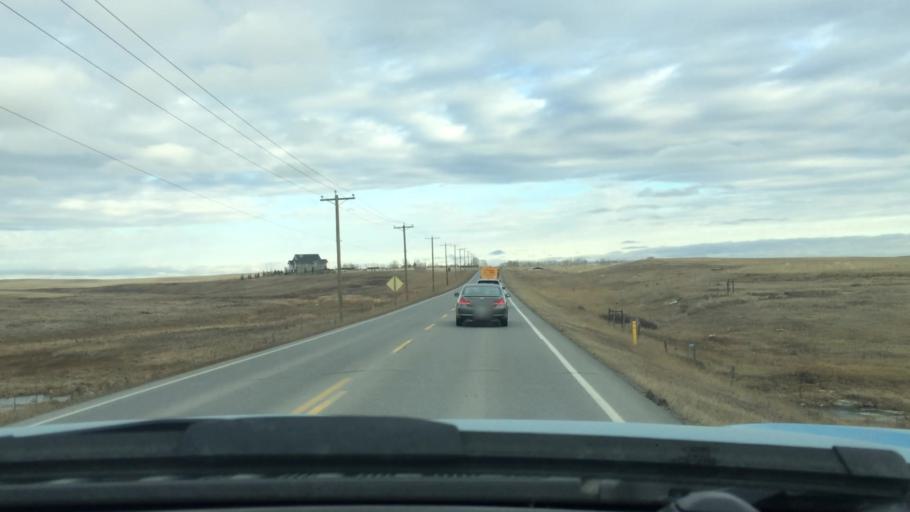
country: CA
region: Alberta
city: Airdrie
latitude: 51.2154
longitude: -114.0249
